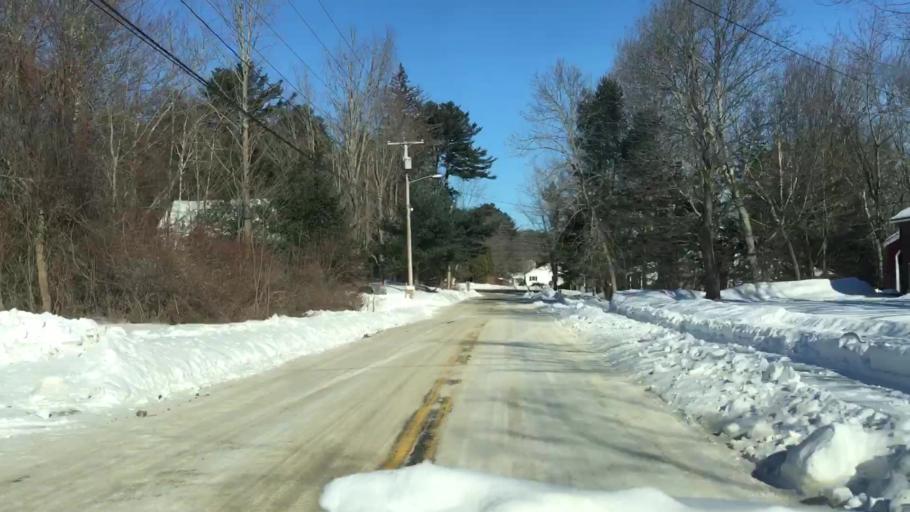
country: US
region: Maine
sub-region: Sagadahoc County
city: Topsham
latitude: 43.9251
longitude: -69.9720
